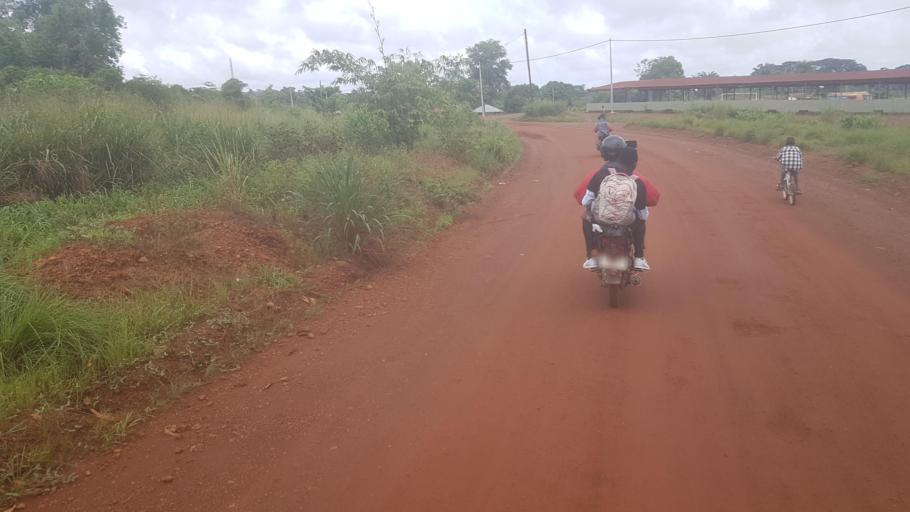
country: SL
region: Southern Province
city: Mogbwemo
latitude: 7.7658
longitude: -12.3015
